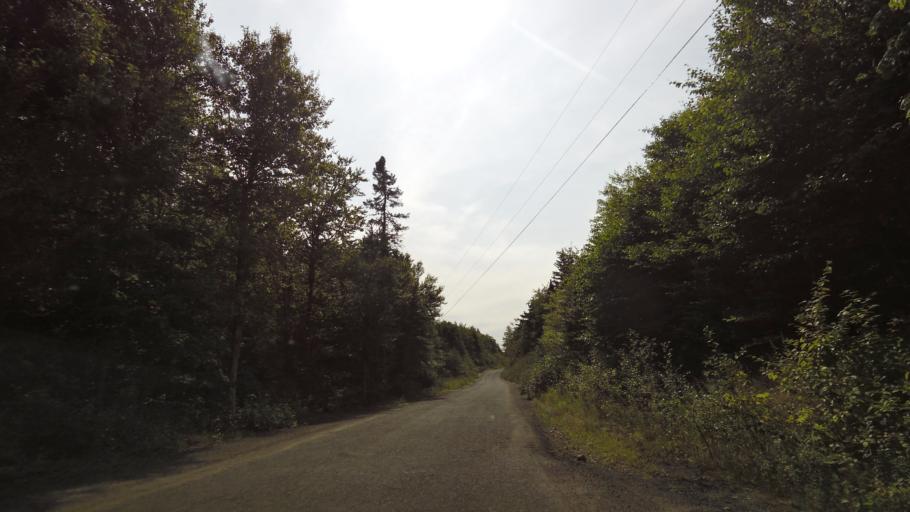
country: CA
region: New Brunswick
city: Hampton
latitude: 45.5702
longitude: -65.8340
